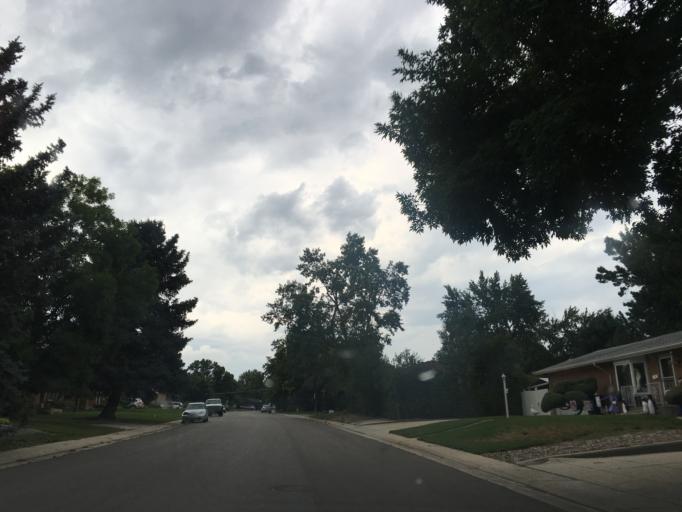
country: US
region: Colorado
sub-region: Arapahoe County
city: Sheridan
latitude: 39.6599
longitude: -105.0371
